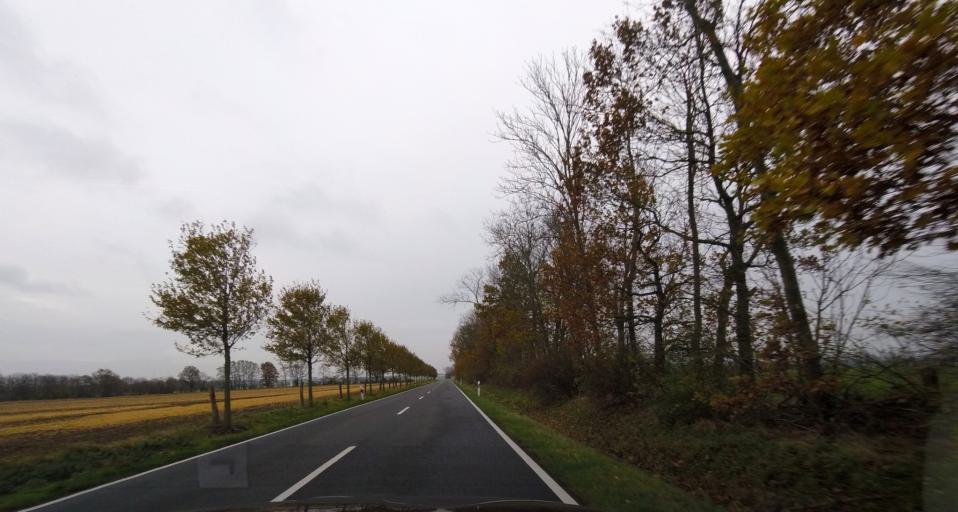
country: DE
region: Saxony-Anhalt
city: Kropstadt
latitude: 52.0207
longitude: 12.7448
